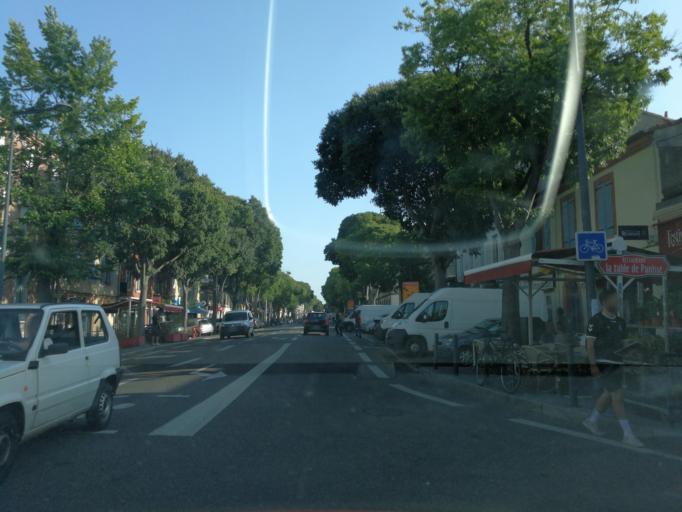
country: FR
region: Midi-Pyrenees
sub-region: Departement de la Haute-Garonne
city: Toulouse
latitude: 43.6202
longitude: 1.4359
